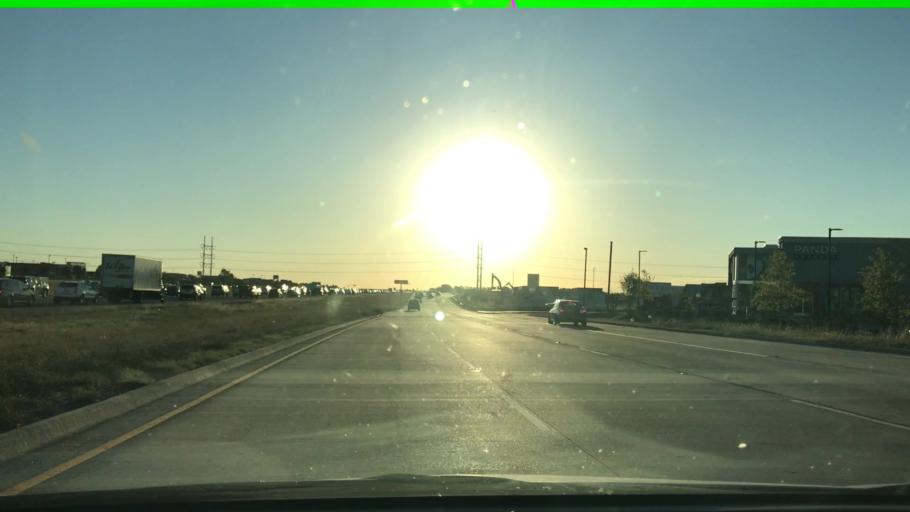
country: US
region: Texas
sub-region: Dallas County
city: Coppell
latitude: 32.9220
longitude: -96.9896
